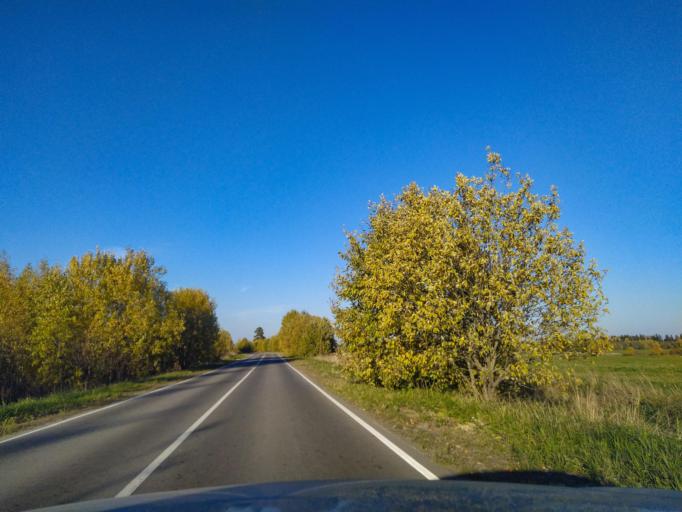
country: RU
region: Leningrad
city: Siverskiy
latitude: 59.3113
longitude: 30.0308
